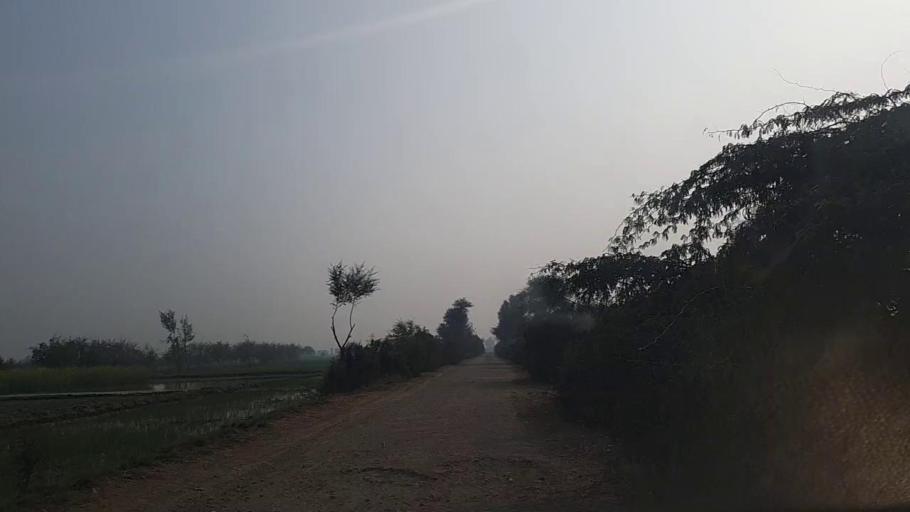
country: PK
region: Sindh
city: Sanghar
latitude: 26.0838
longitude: 68.9203
